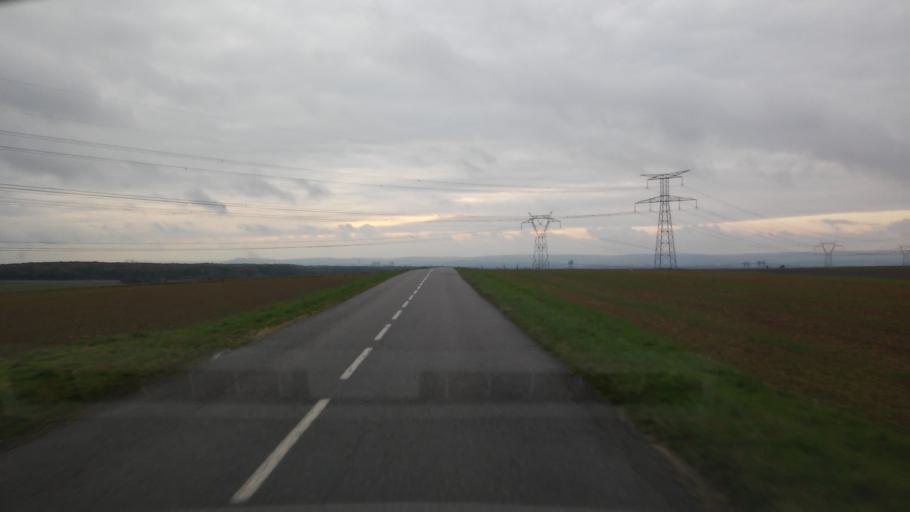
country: FR
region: Lorraine
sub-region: Departement de la Moselle
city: Vigy
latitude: 49.1882
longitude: 6.3265
